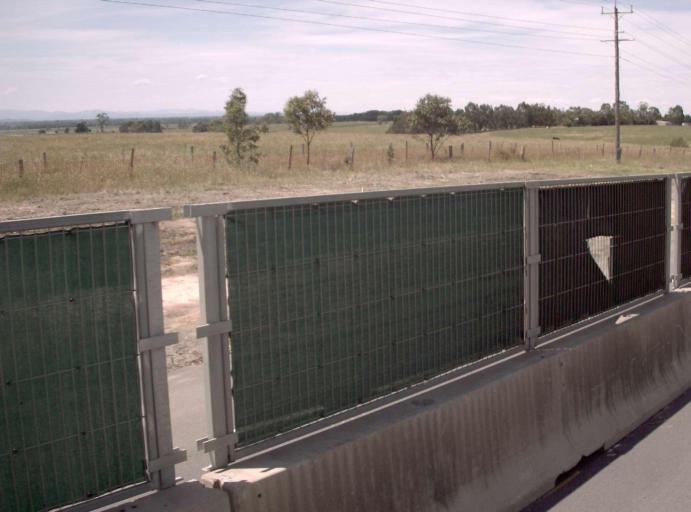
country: AU
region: Victoria
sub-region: Latrobe
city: Traralgon
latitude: -38.1880
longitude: 146.5773
